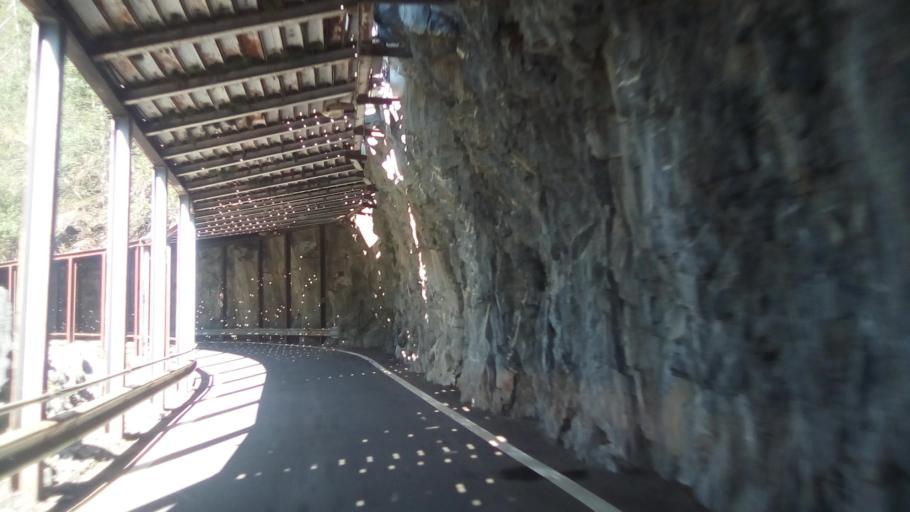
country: CH
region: Valais
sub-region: Saint-Maurice District
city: Salvan
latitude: 46.1040
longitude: 7.0000
